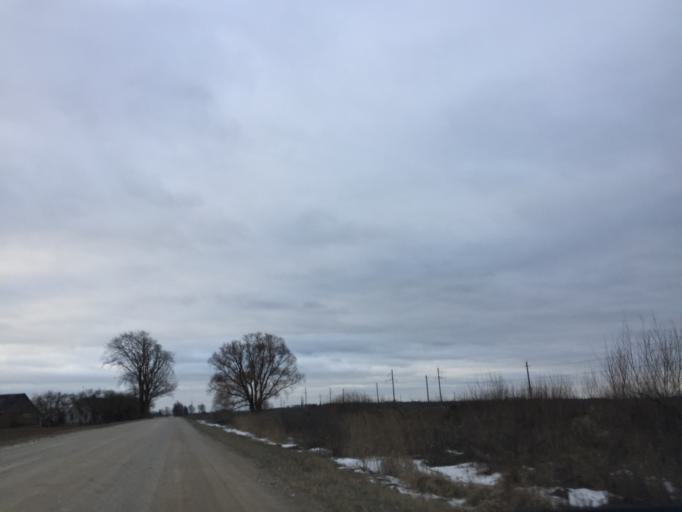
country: LT
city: Zagare
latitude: 56.3457
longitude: 23.2515
